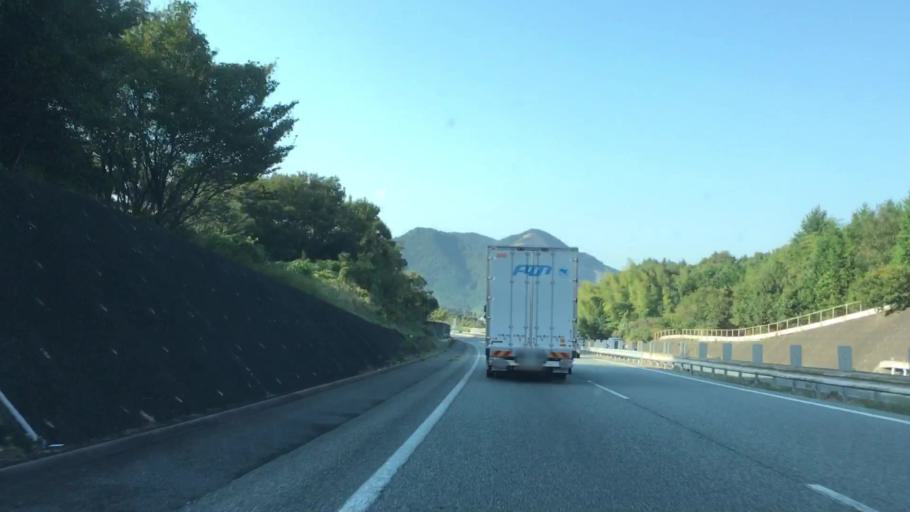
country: JP
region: Yamaguchi
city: Hofu
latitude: 34.0647
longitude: 131.5013
